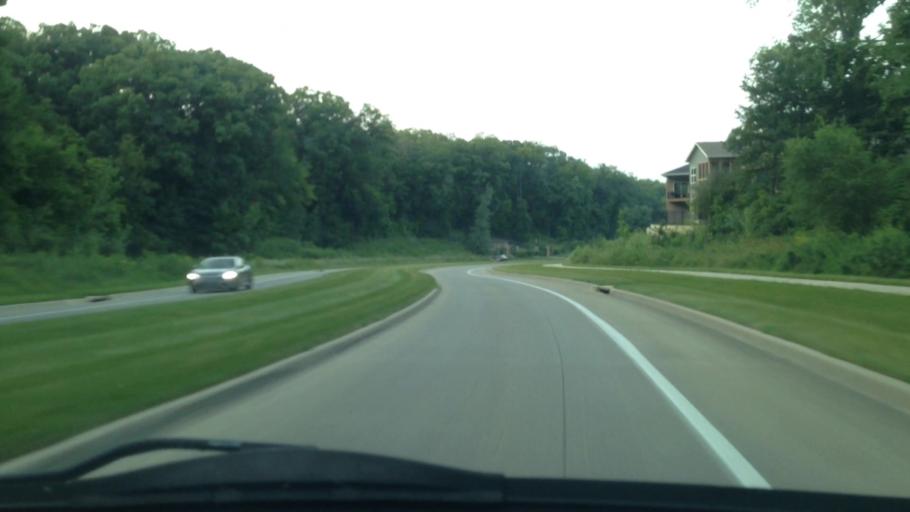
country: US
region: Iowa
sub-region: Johnson County
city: Coralville
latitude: 41.6709
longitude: -91.6035
